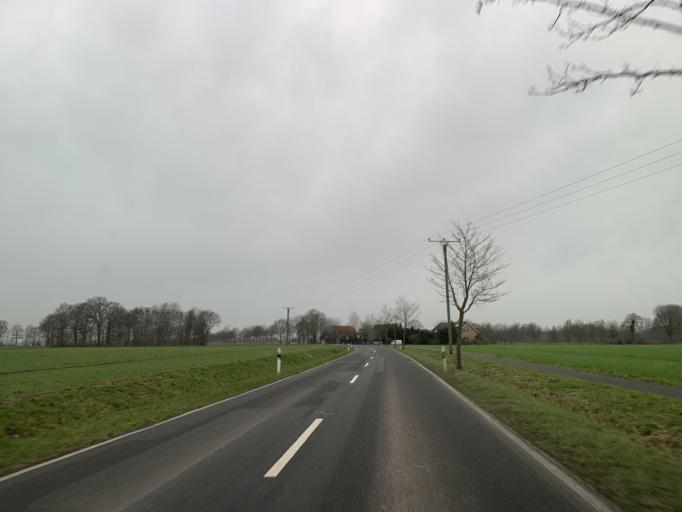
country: DE
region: North Rhine-Westphalia
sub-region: Regierungsbezirk Munster
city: Senden
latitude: 51.8542
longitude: 7.4484
